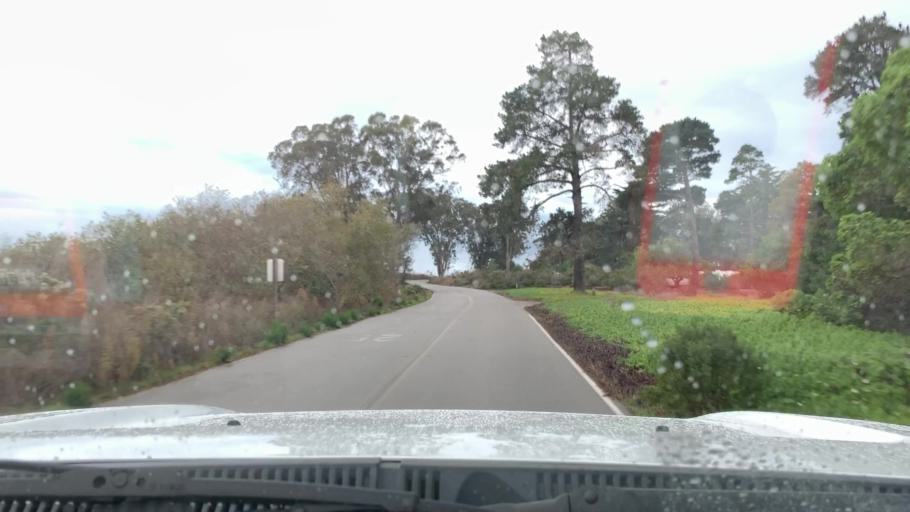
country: US
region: California
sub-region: San Luis Obispo County
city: Morro Bay
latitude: 35.3466
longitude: -120.8369
